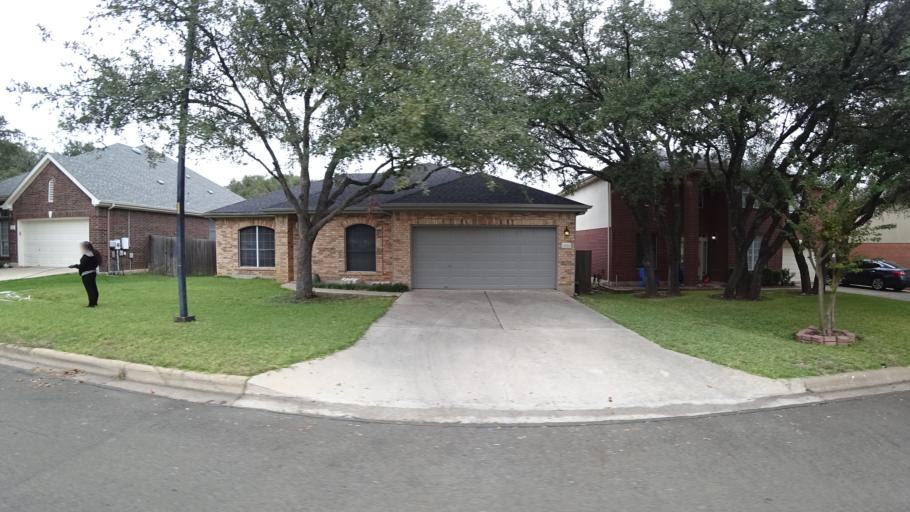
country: US
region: Texas
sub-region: Travis County
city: Shady Hollow
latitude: 30.2116
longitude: -97.8877
